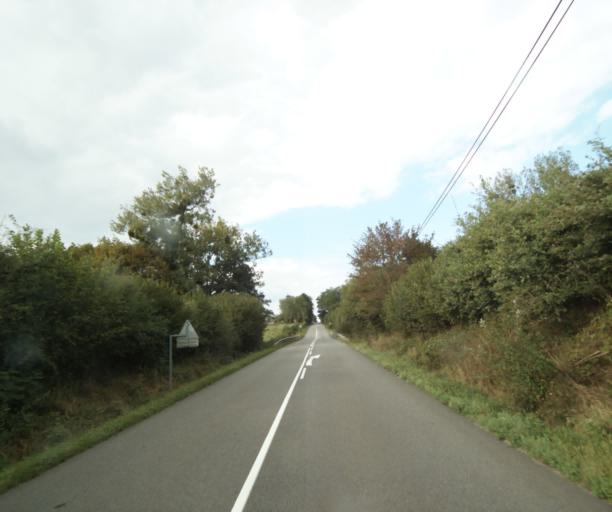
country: FR
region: Bourgogne
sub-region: Departement de Saone-et-Loire
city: Palinges
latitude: 46.5192
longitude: 4.2552
